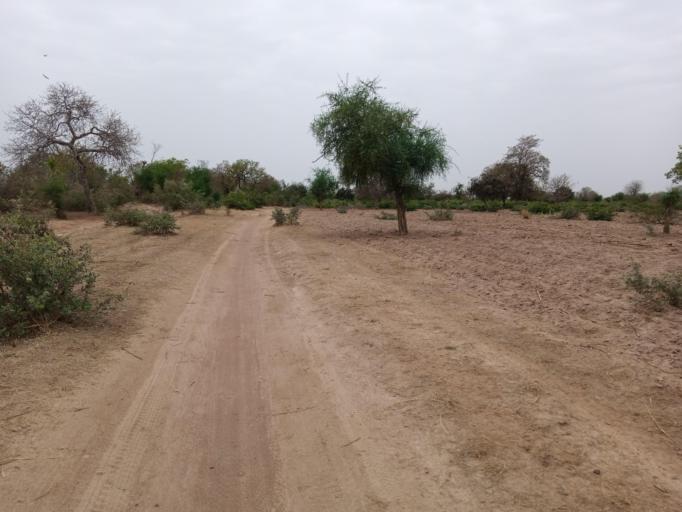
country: BF
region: Boucle du Mouhoun
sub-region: Province de la Kossi
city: Nouna
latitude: 12.8316
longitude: -4.0771
